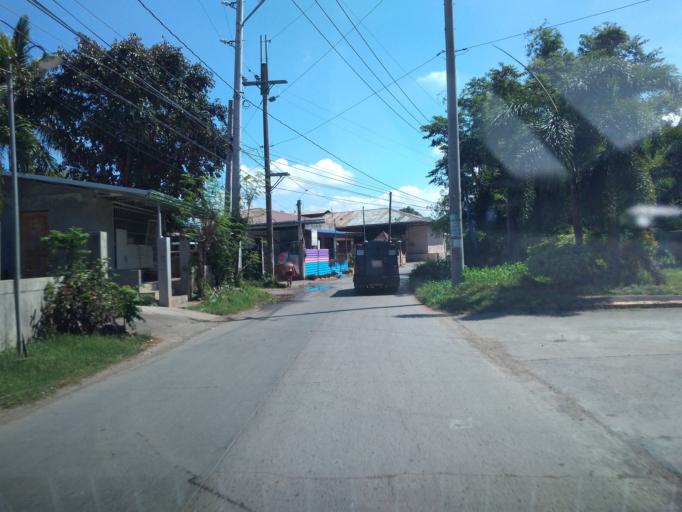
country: PH
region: Central Luzon
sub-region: Province of Bulacan
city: Bitungol
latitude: 14.8602
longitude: 121.0360
